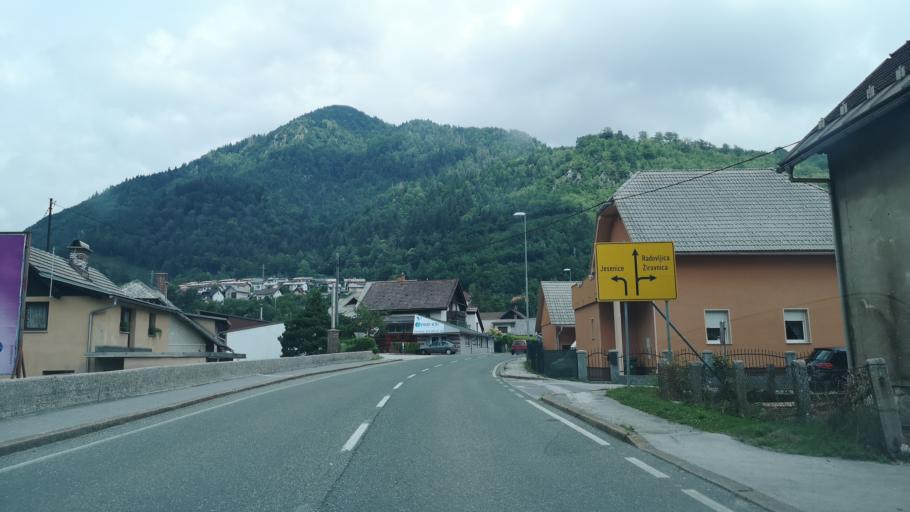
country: SI
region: Jesenice
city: Slovenski Javornik
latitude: 46.4257
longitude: 14.0816
